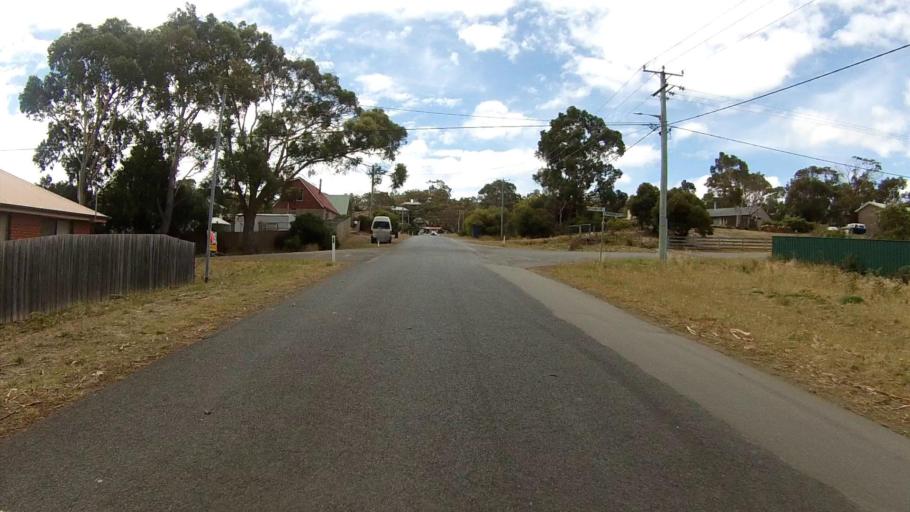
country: AU
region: Tasmania
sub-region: Sorell
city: Sorell
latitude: -42.8690
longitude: 147.6444
